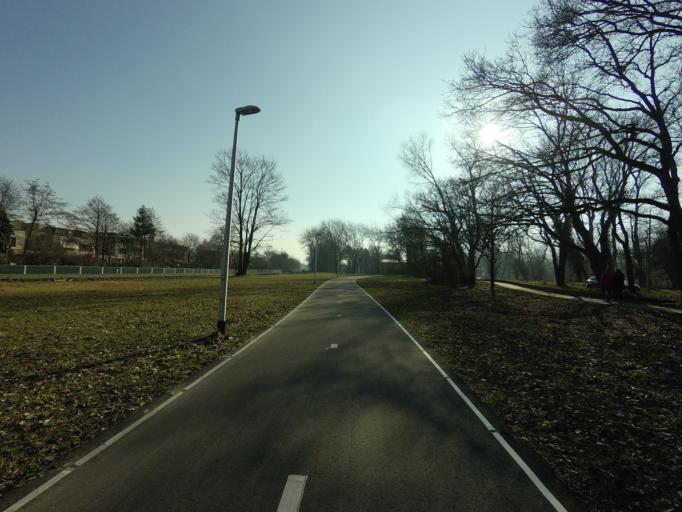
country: NL
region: North Holland
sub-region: Gemeente Velsen
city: Velsen-Zuid
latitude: 52.4428
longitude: 4.6320
